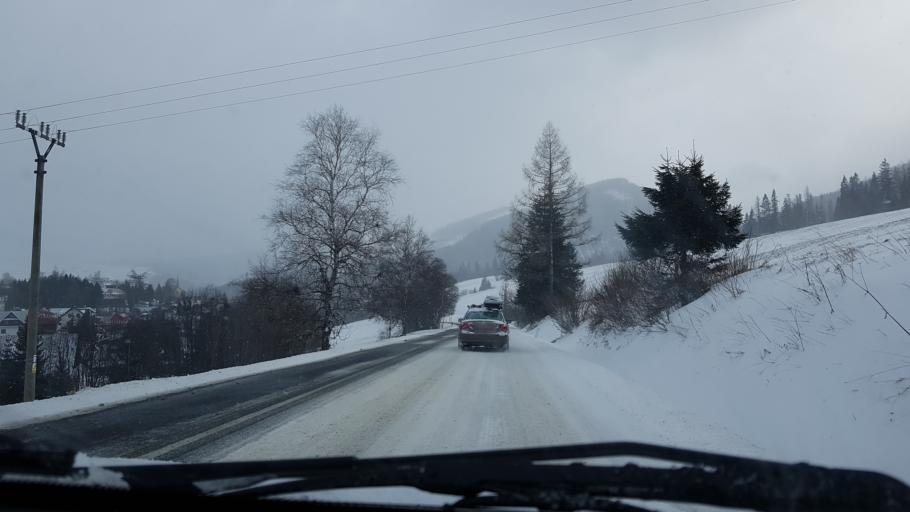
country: SK
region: Presovsky
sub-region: Okres Poprad
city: Zdiar
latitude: 49.2726
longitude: 20.2523
